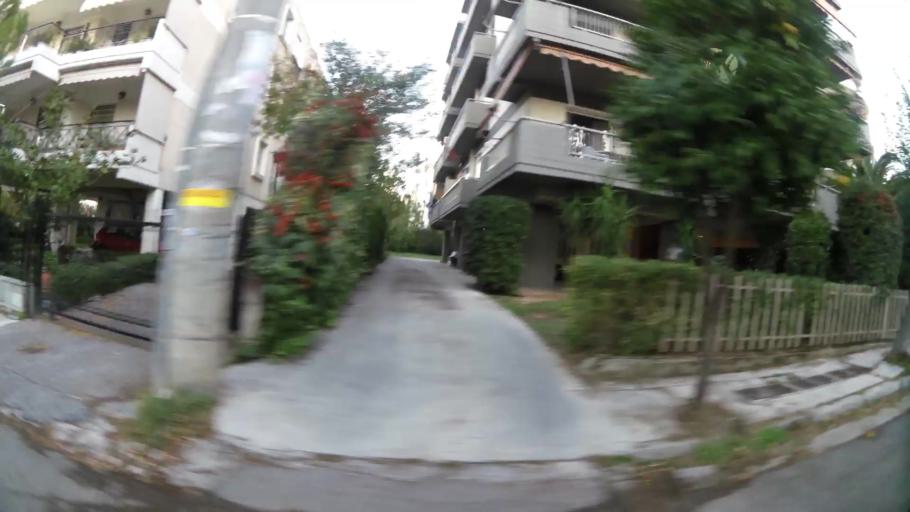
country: GR
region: Attica
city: Pefki
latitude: 38.0619
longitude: 23.7923
